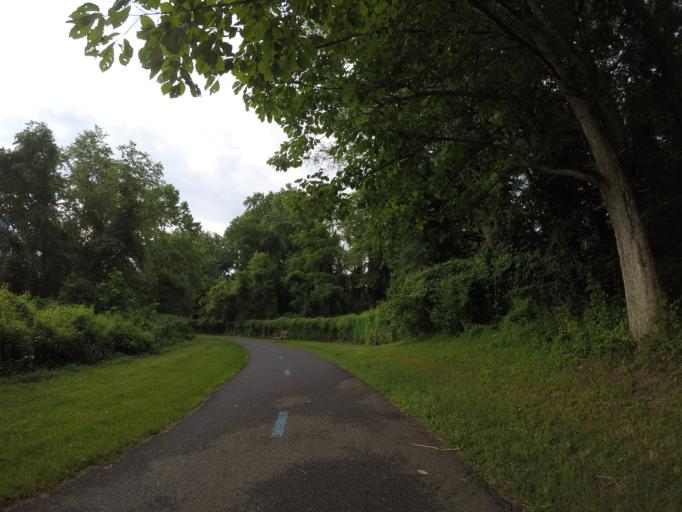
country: US
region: Maryland
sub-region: Prince George's County
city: College Park
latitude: 38.9839
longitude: -76.9226
